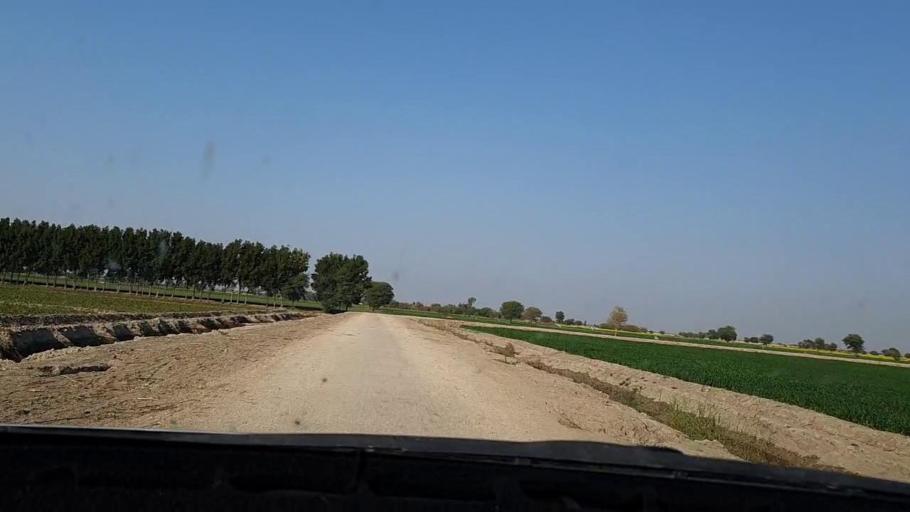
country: PK
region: Sindh
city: Tando Mittha Khan
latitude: 25.8272
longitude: 69.3064
